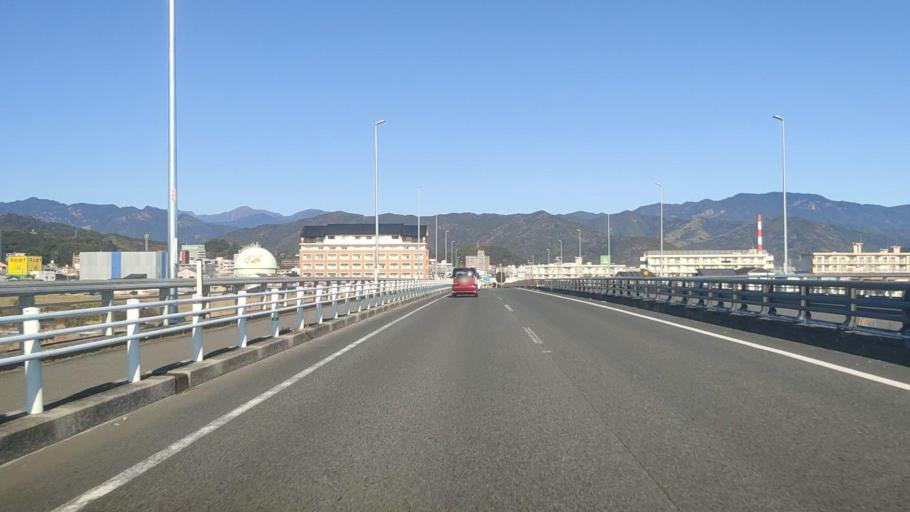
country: JP
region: Miyazaki
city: Nobeoka
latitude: 32.5835
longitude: 131.6795
